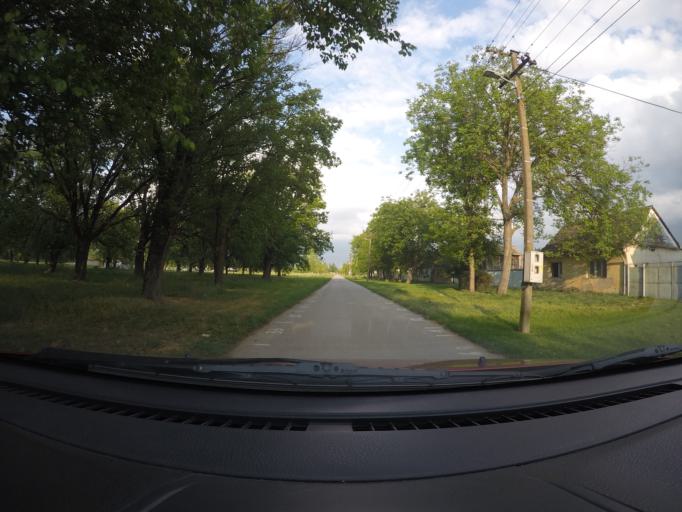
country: RS
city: Debeljaca
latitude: 45.0634
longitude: 20.6064
